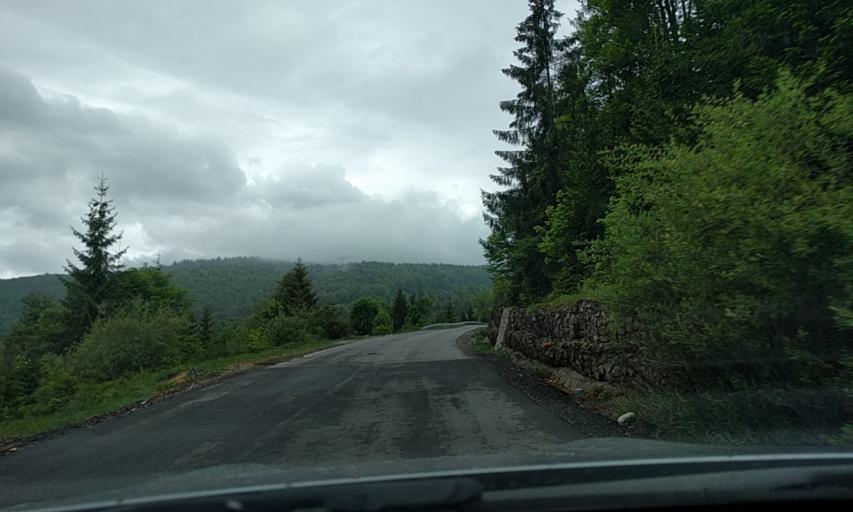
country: RO
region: Prahova
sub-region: Oras Sinaia
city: Sinaia
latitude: 45.3002
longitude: 25.5211
